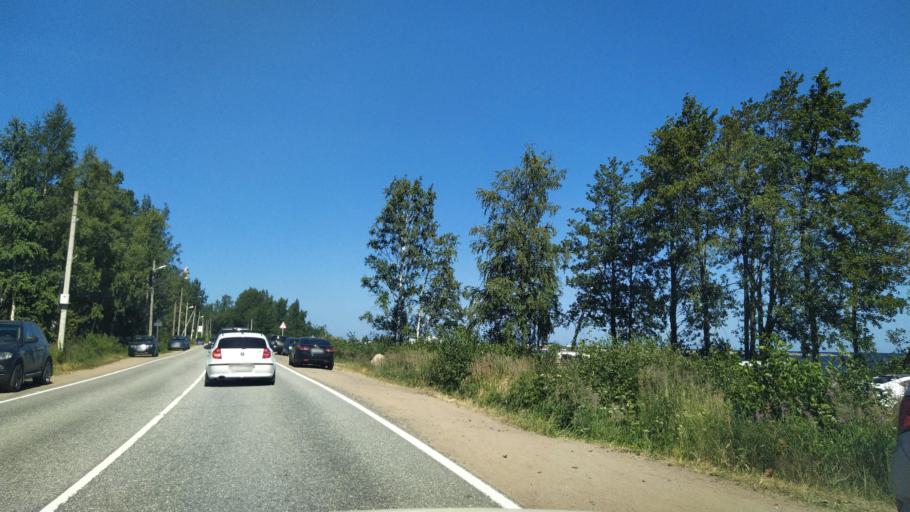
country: RU
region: Leningrad
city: Borisova Griva
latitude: 60.1125
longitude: 31.0845
